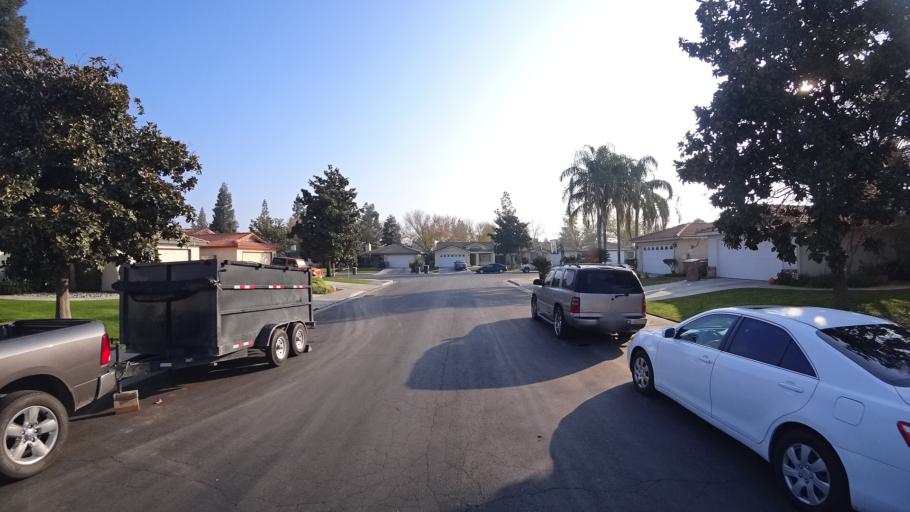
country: US
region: California
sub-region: Kern County
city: Greenacres
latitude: 35.3240
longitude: -119.0933
